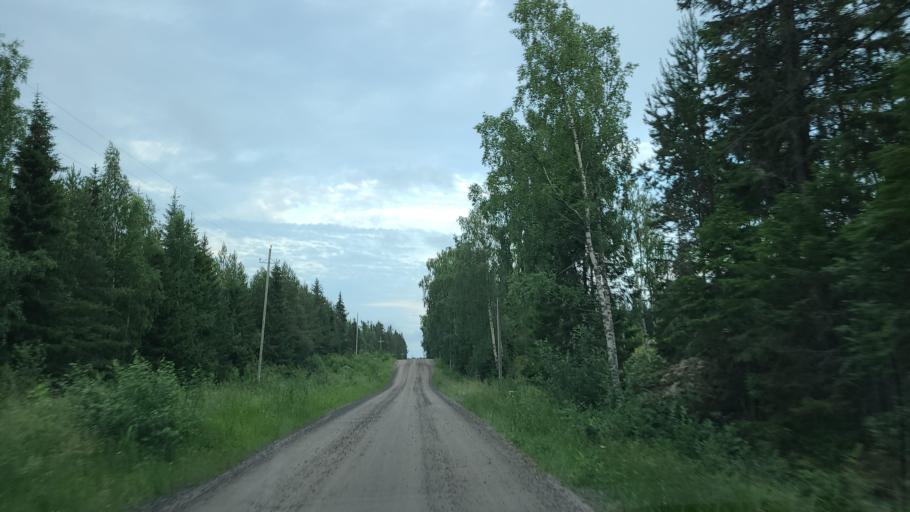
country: FI
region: Ostrobothnia
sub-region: Vaasa
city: Replot
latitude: 63.3220
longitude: 21.1420
